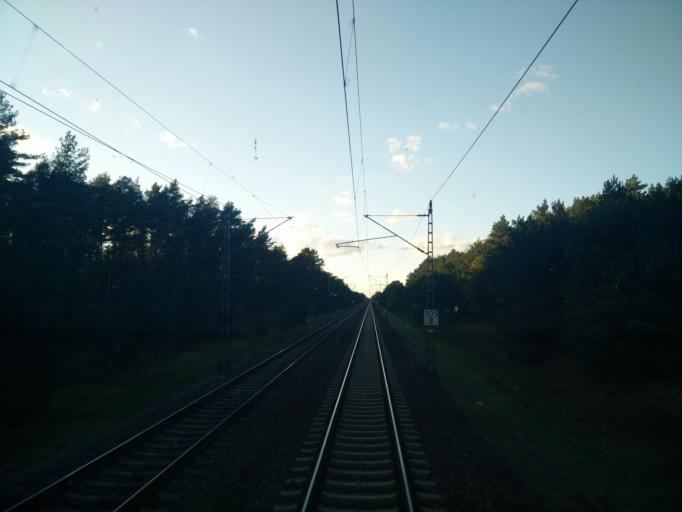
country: DE
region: Brandenburg
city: Plattenburg
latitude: 52.9232
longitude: 12.0353
